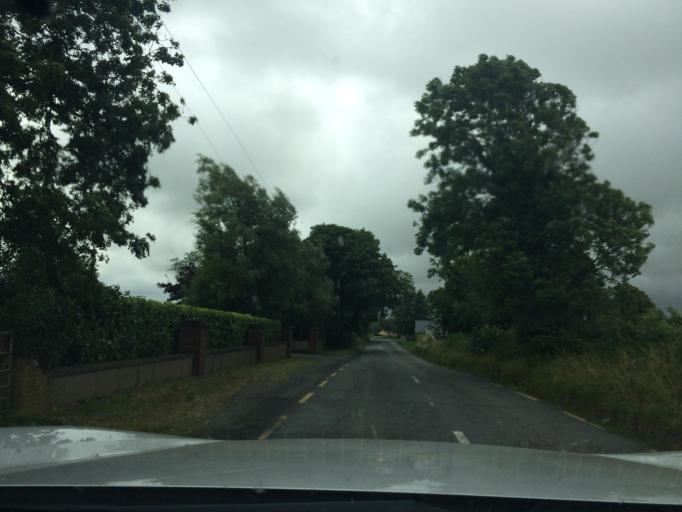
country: IE
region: Munster
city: Cashel
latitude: 52.4862
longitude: -7.8556
